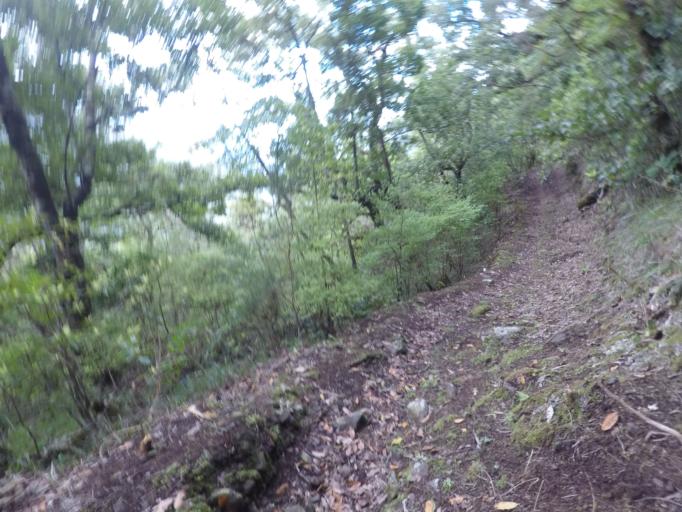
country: PT
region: Madeira
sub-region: Camara de Lobos
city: Curral das Freiras
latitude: 32.7707
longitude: -16.9788
